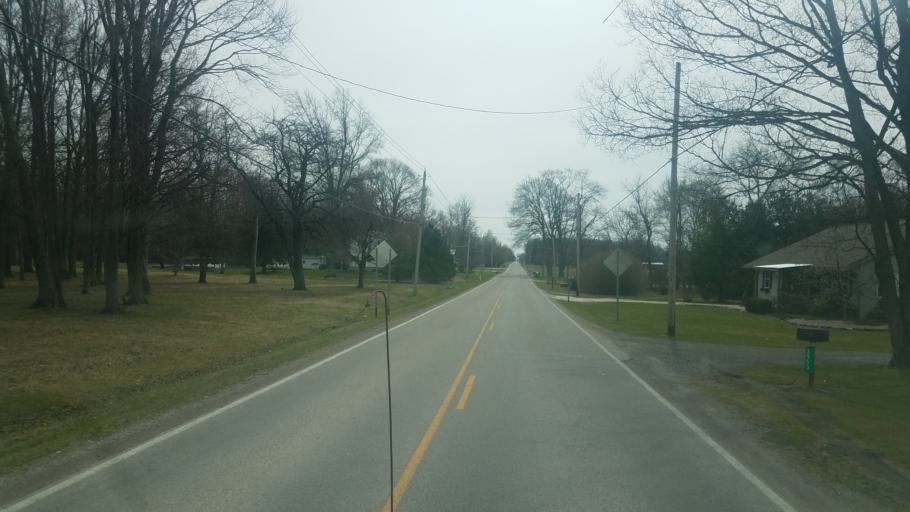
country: US
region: Ohio
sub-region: Huron County
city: Wakeman
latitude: 41.2464
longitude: -82.4916
